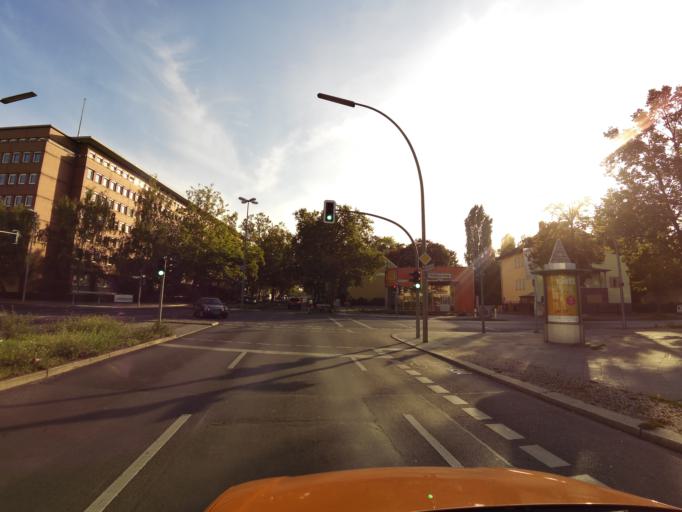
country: DE
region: Berlin
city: Wilmersdorf Bezirk
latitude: 52.4924
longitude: 13.3094
